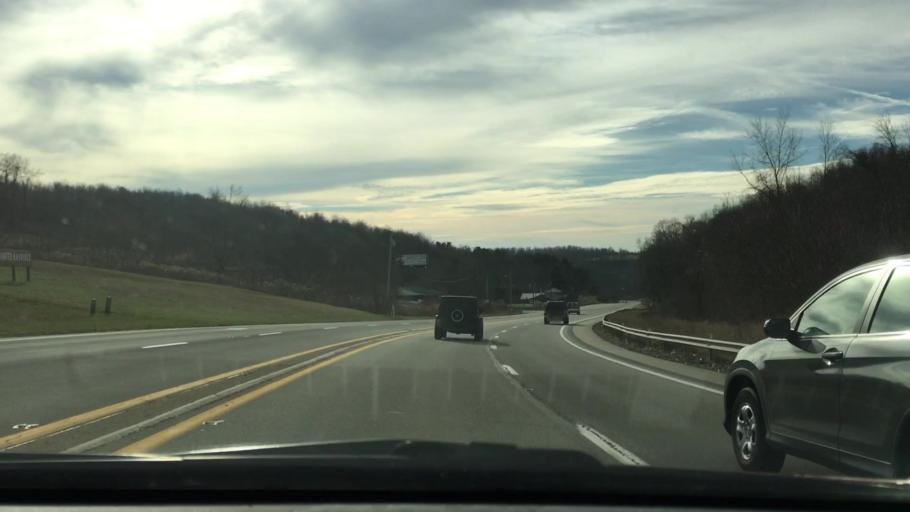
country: US
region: Pennsylvania
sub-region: Fayette County
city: Perryopolis
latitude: 40.0210
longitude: -79.7653
